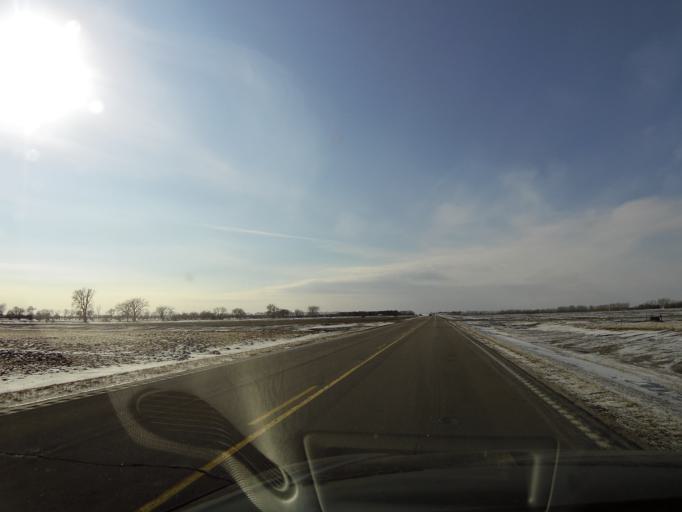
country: US
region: North Dakota
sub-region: Walsh County
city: Grafton
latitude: 48.4121
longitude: -97.1670
